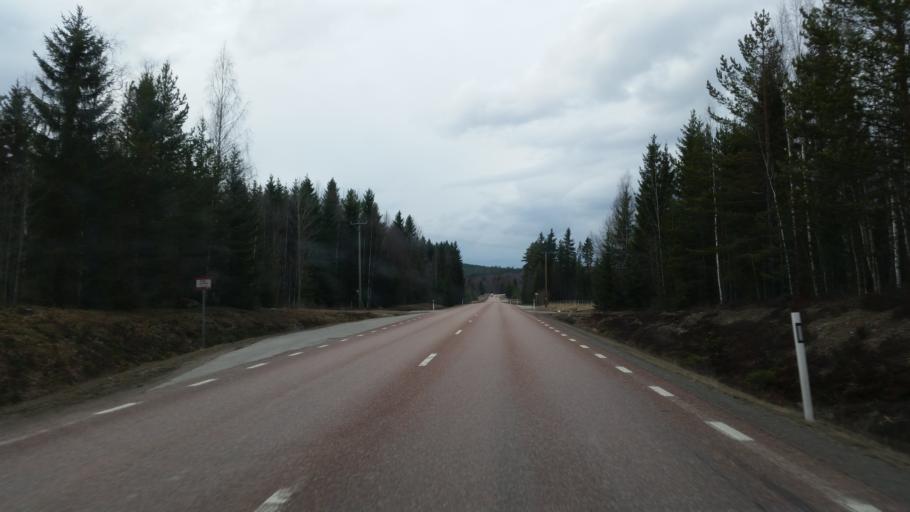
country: SE
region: Gaevleborg
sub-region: Ljusdals Kommun
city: Ljusdal
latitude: 61.7812
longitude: 16.1404
